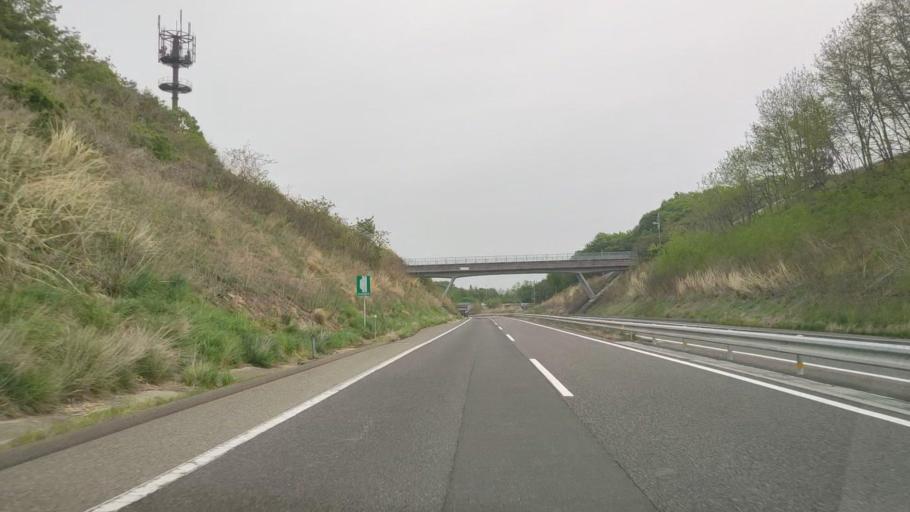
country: JP
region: Fukushima
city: Motomiya
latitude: 37.4584
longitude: 140.4062
